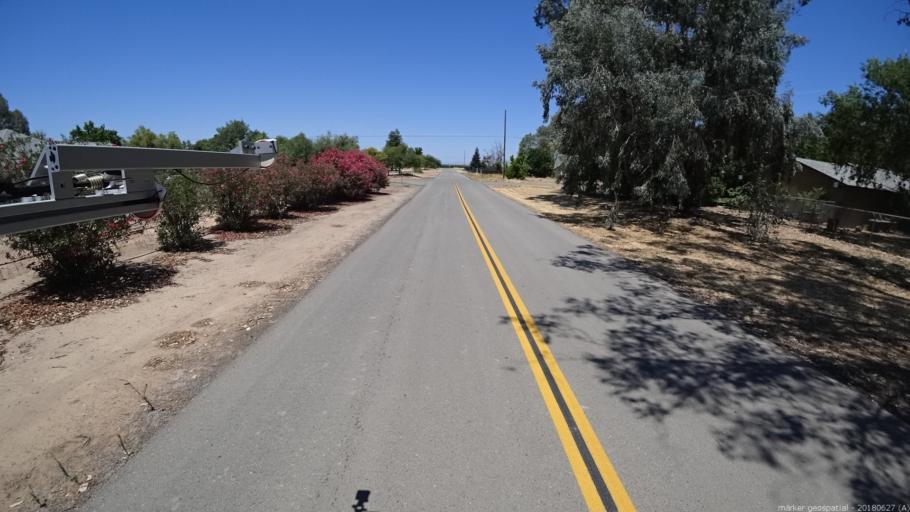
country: US
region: California
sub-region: Madera County
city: Bonadelle Ranchos-Madera Ranchos
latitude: 36.9348
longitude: -119.8881
